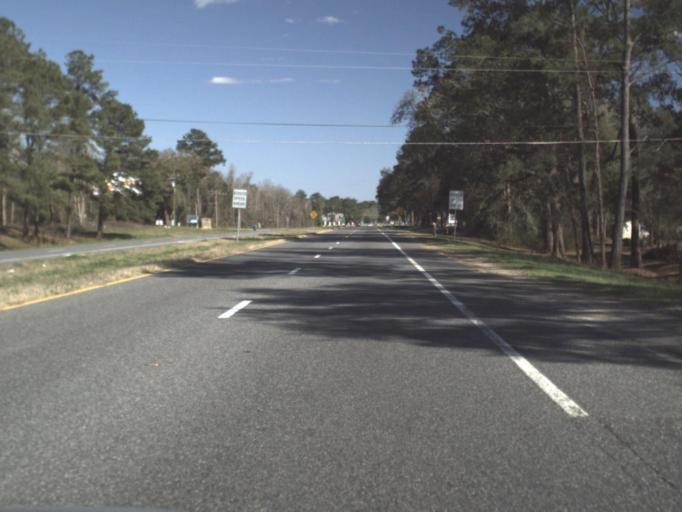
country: US
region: Florida
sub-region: Gadsden County
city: Midway
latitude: 30.4962
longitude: -84.4365
